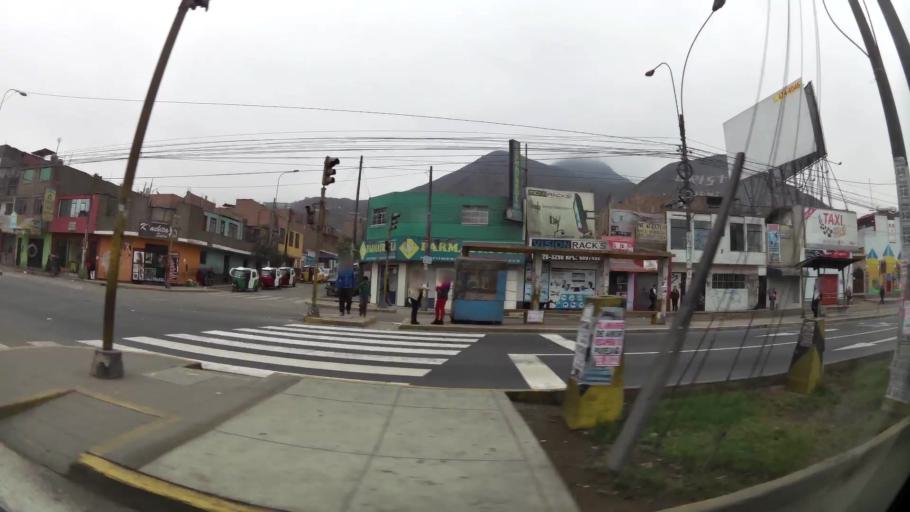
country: PE
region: Lima
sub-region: Lima
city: Independencia
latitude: -11.9488
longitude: -77.0494
